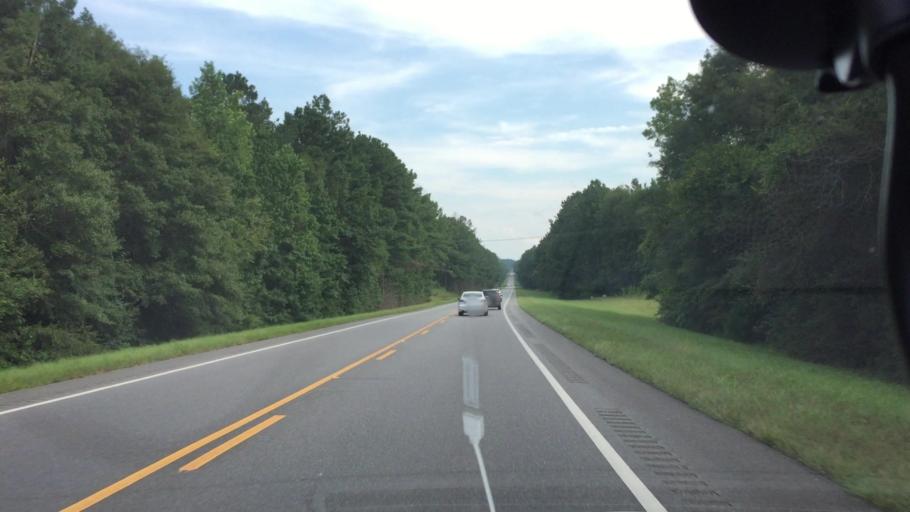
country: US
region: Alabama
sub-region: Pike County
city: Brundidge
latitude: 31.5739
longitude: -85.9293
